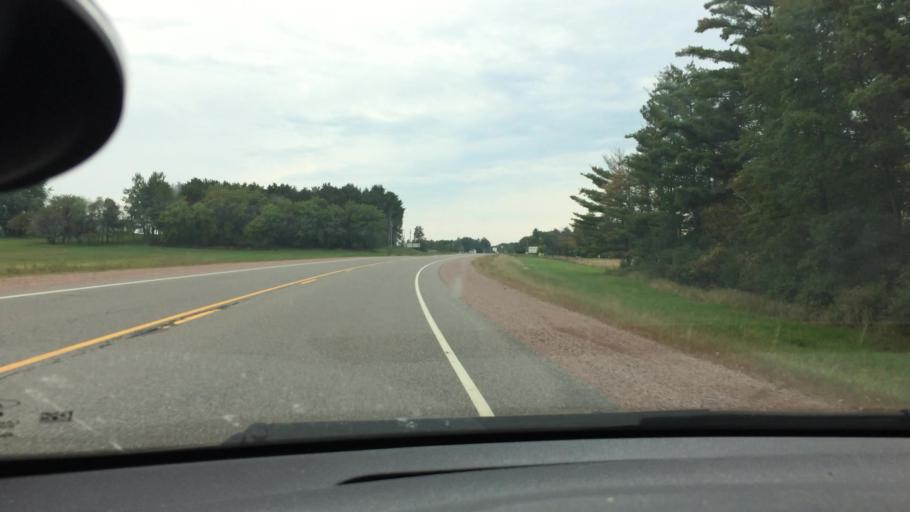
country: US
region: Wisconsin
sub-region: Clark County
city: Neillsville
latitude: 44.5627
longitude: -90.6853
